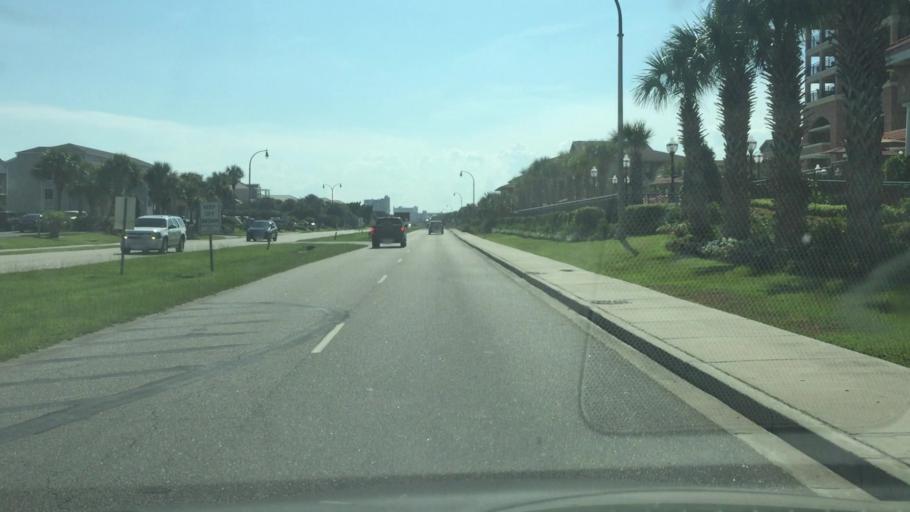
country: US
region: South Carolina
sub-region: Horry County
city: North Myrtle Beach
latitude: 33.8266
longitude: -78.6494
